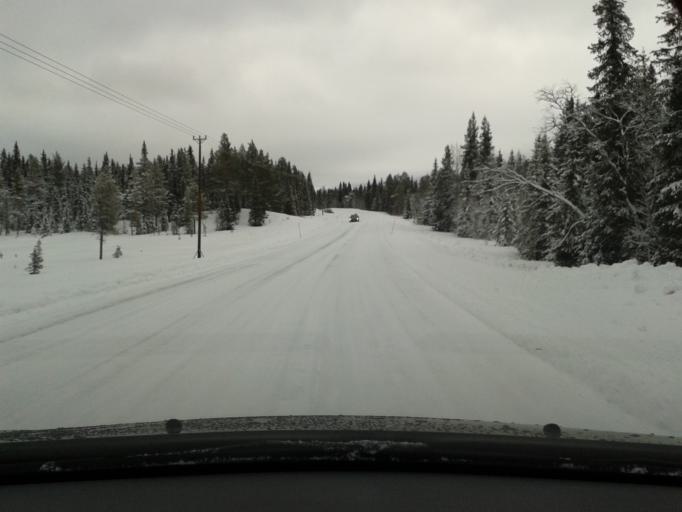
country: SE
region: Vaesterbotten
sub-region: Vilhelmina Kommun
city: Sjoberg
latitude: 65.2380
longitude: 15.8082
